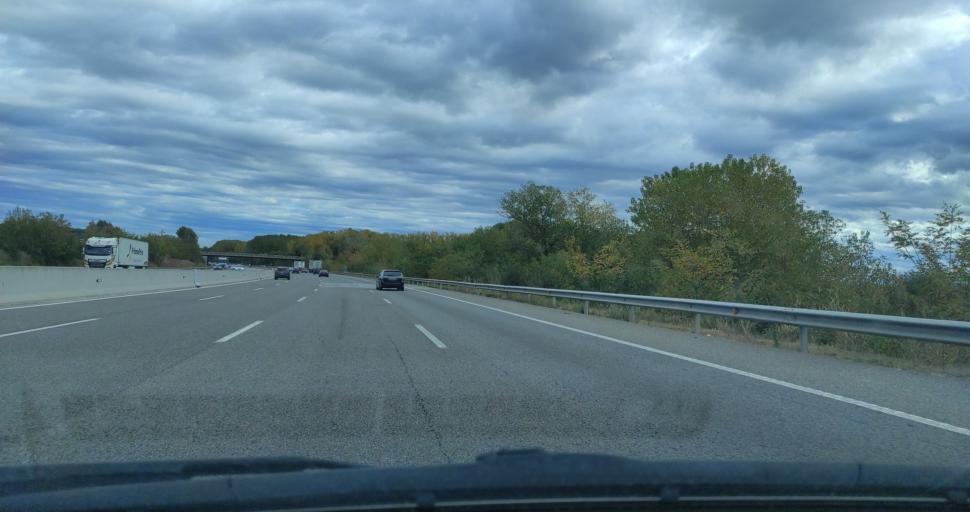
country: ES
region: Catalonia
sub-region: Provincia de Girona
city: Sant Julia de Ramis
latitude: 42.0448
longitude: 2.8633
